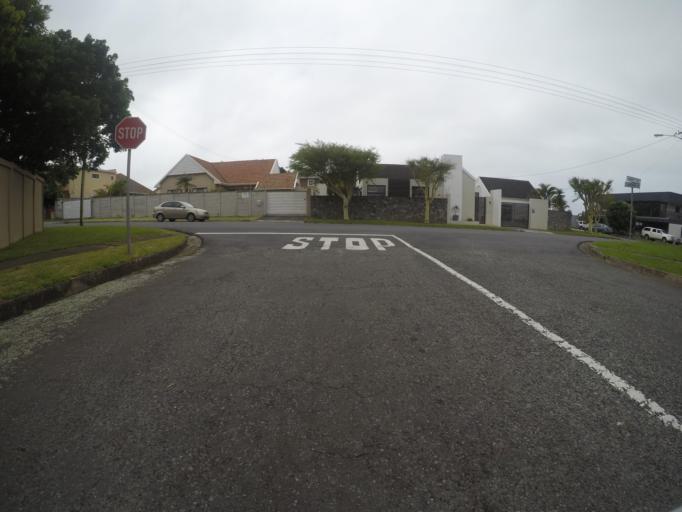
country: ZA
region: Eastern Cape
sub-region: Buffalo City Metropolitan Municipality
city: East London
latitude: -32.9889
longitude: 27.9333
